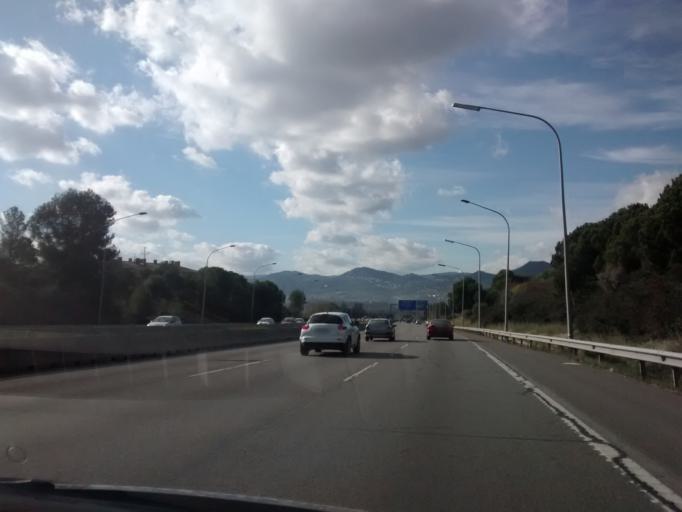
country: ES
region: Catalonia
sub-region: Provincia de Barcelona
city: Sant Joan Despi
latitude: 41.3750
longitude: 2.0604
